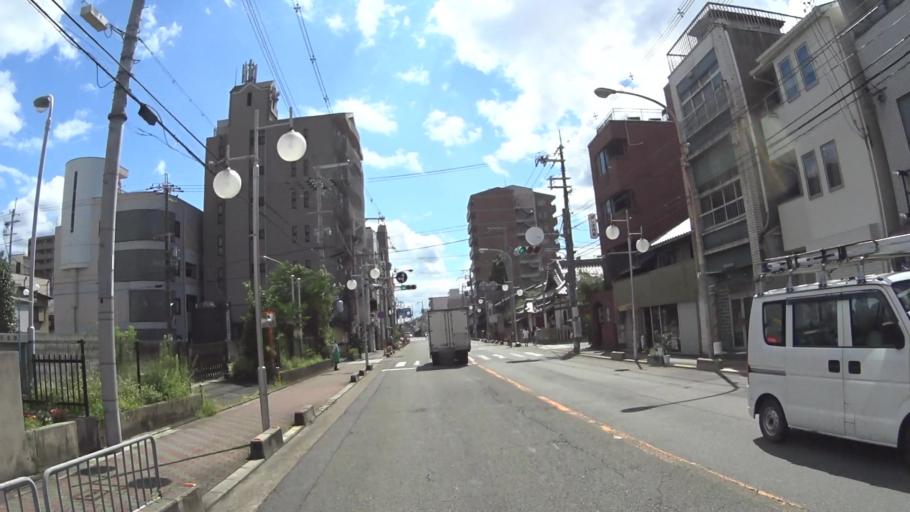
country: JP
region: Kyoto
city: Kyoto
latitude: 34.9812
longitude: 135.7610
